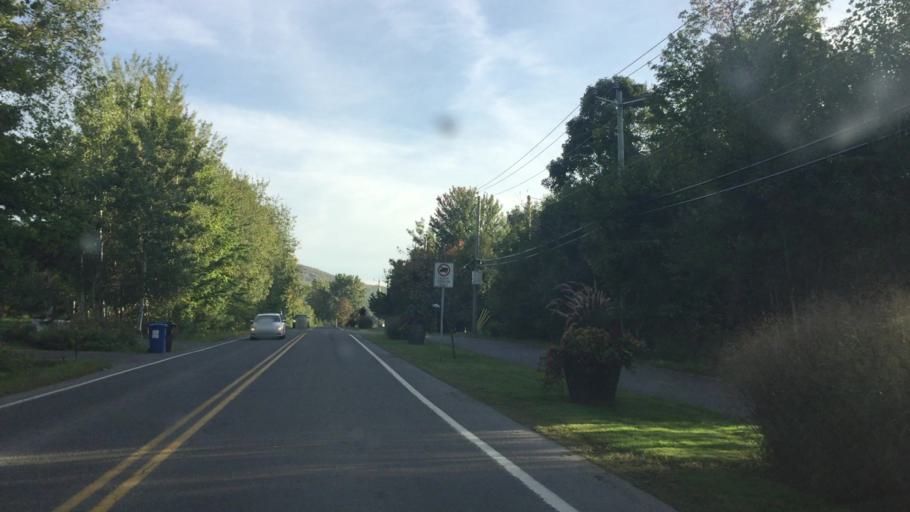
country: CA
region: Quebec
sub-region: Monteregie
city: Bromont
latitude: 45.3120
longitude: -72.6573
